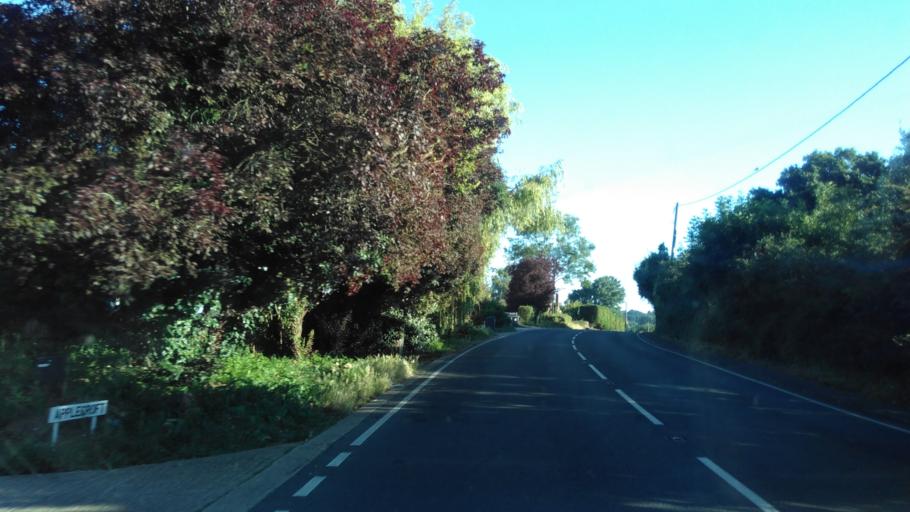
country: GB
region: England
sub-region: Kent
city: Blean
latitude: 51.3288
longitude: 1.0247
